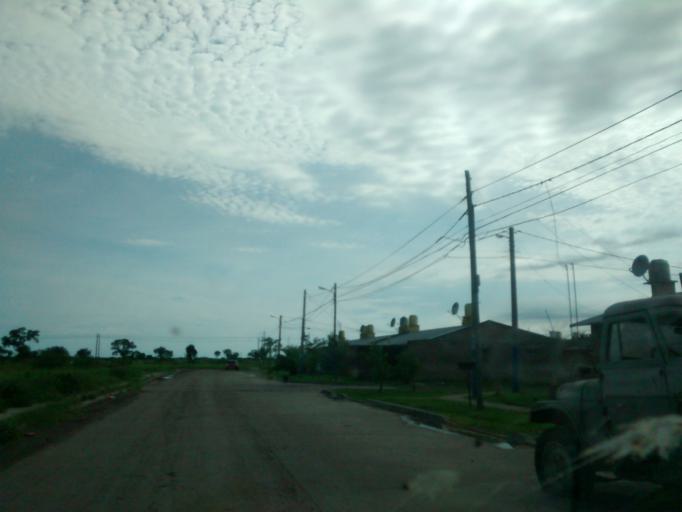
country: AR
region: Chaco
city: Resistencia
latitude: -27.4107
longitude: -58.9620
